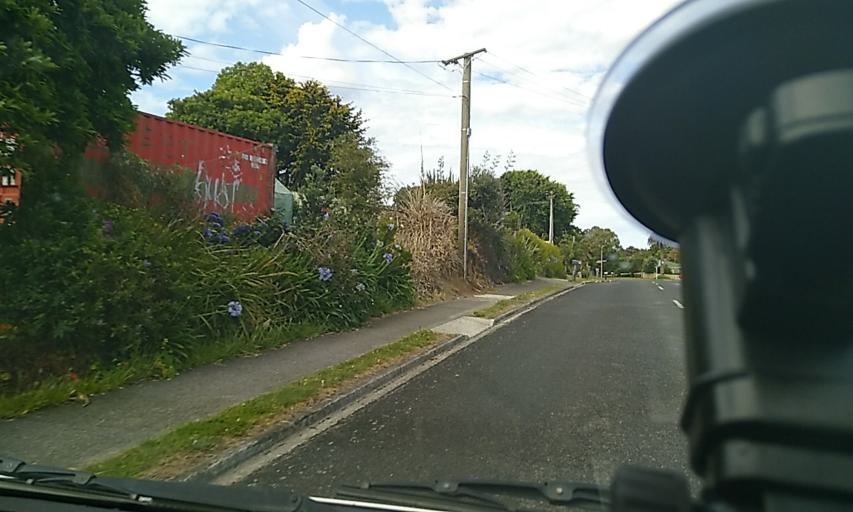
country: NZ
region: Bay of Plenty
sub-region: Western Bay of Plenty District
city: Waihi Beach
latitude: -37.4459
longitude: 175.9610
